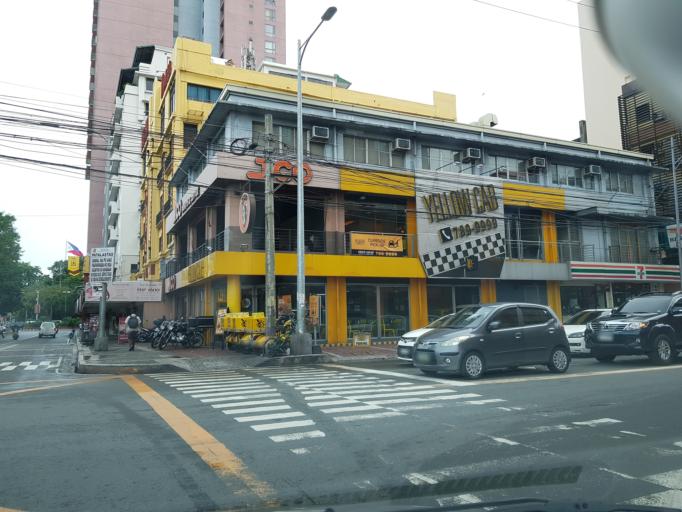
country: PH
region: Metro Manila
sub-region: City of Manila
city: Port Area
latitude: 14.5789
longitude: 120.9782
